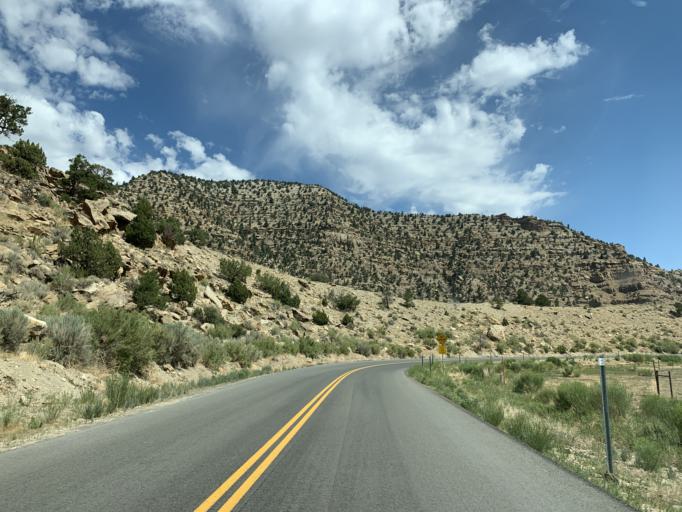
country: US
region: Utah
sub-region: Carbon County
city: East Carbon City
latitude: 39.7997
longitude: -110.3854
